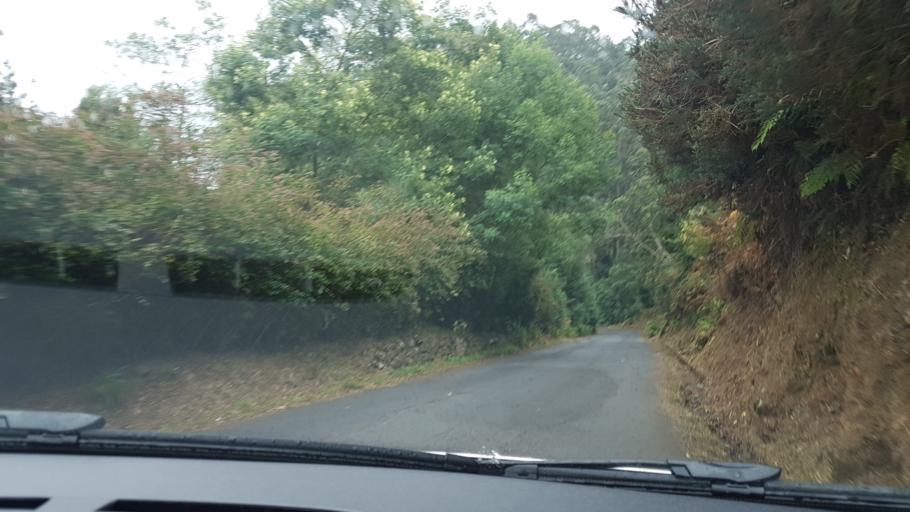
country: PT
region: Madeira
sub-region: Santa Cruz
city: Santa Cruz
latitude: 32.7277
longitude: -16.8134
